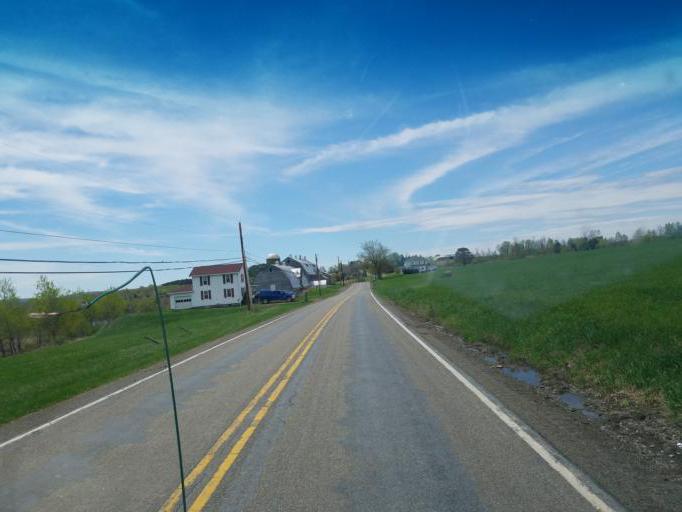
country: US
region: Pennsylvania
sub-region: Tioga County
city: Wellsboro
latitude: 41.7122
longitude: -77.3833
